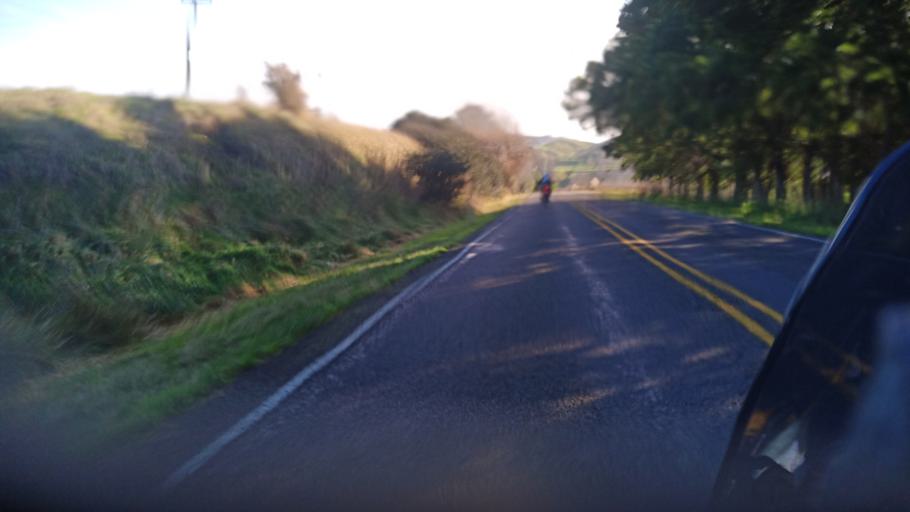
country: NZ
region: Gisborne
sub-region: Gisborne District
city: Gisborne
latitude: -38.4559
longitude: 177.7867
